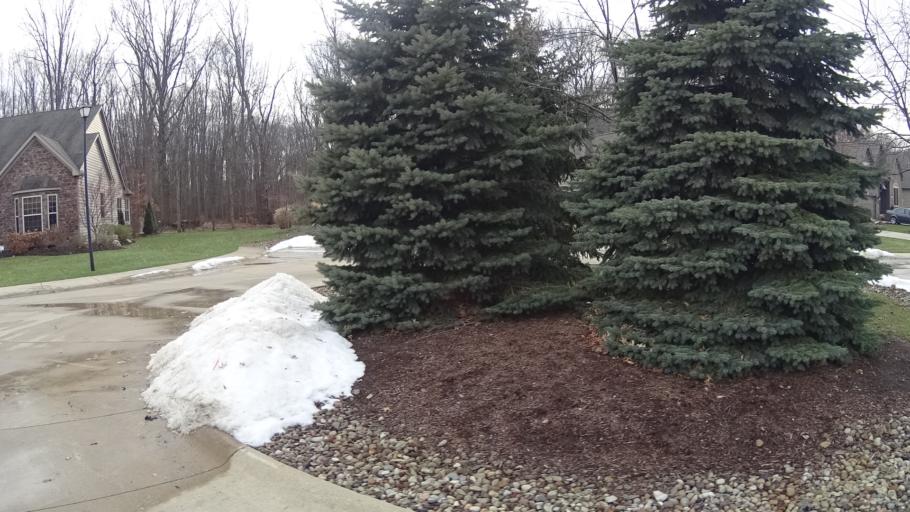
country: US
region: Ohio
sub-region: Lorain County
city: Amherst
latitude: 41.3839
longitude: -82.2322
